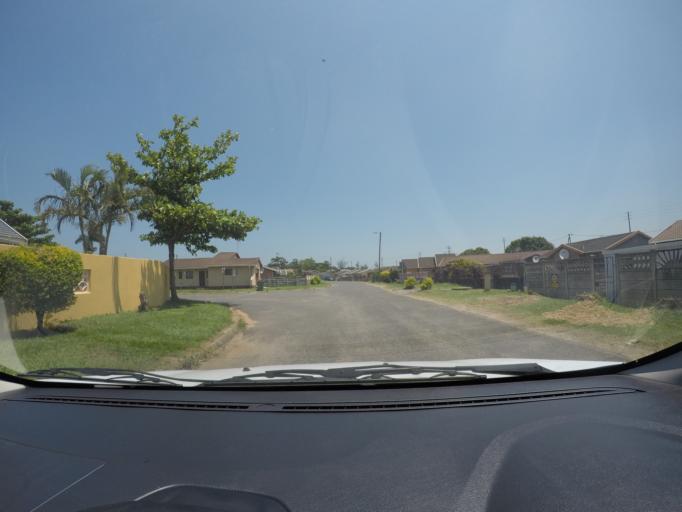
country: ZA
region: KwaZulu-Natal
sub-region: uThungulu District Municipality
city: eSikhawini
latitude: -28.8902
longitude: 31.8817
